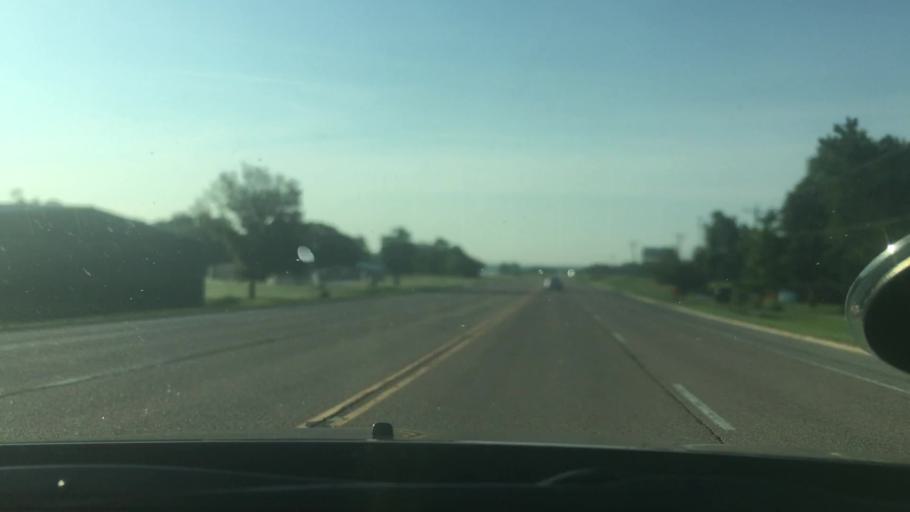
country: US
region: Oklahoma
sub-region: Pontotoc County
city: Ada
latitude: 34.7904
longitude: -96.7299
